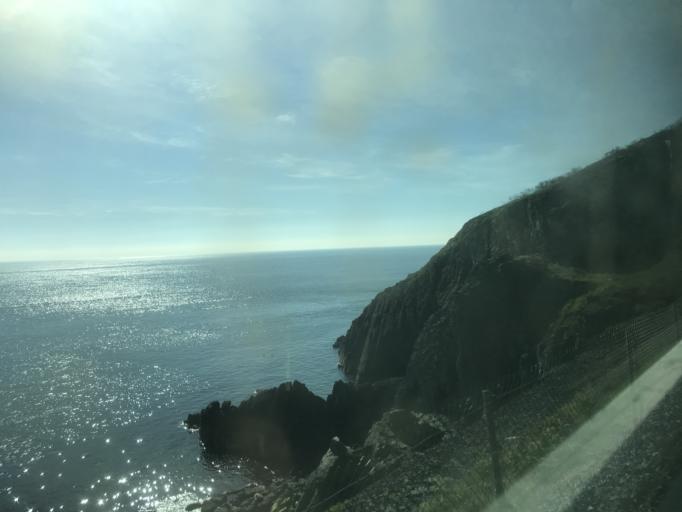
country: IE
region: Leinster
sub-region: Wicklow
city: Bray
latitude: 53.1771
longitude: -6.0745
